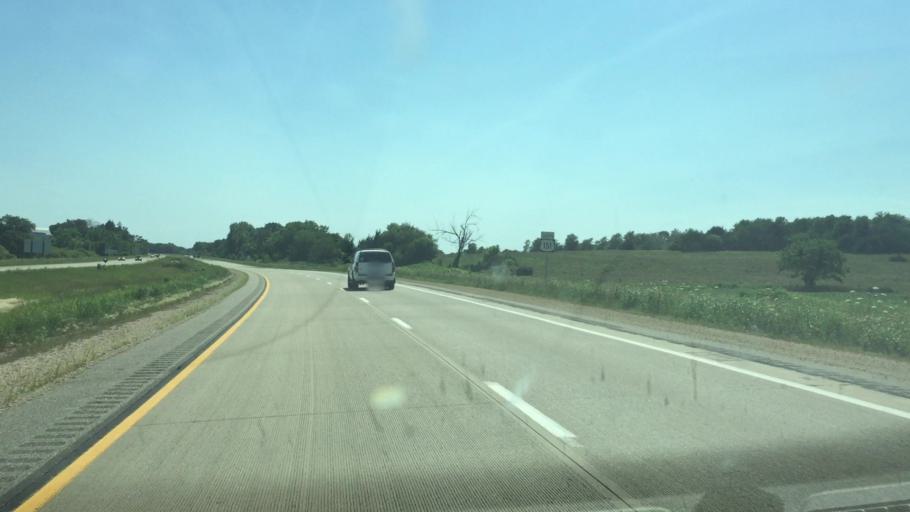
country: US
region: Iowa
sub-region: Jones County
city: Monticello
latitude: 42.2055
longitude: -91.2005
